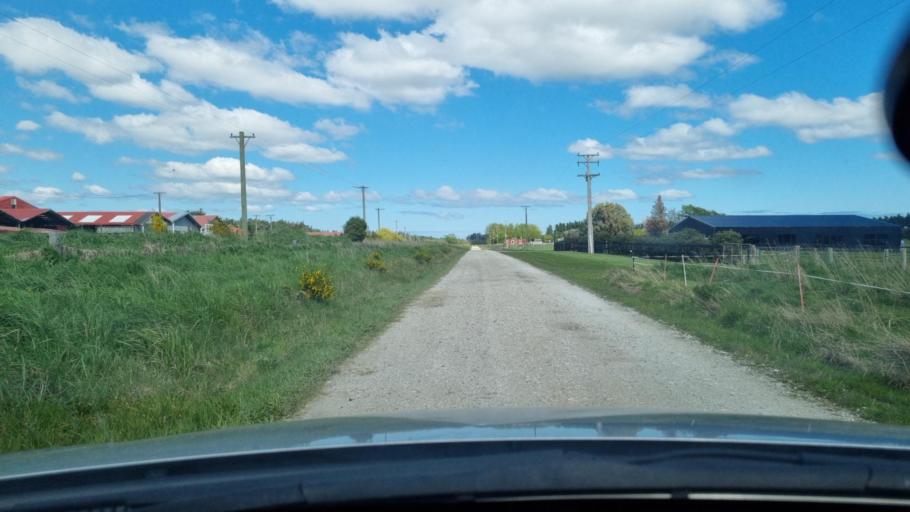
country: NZ
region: Southland
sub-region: Invercargill City
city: Invercargill
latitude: -46.3449
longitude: 168.3401
